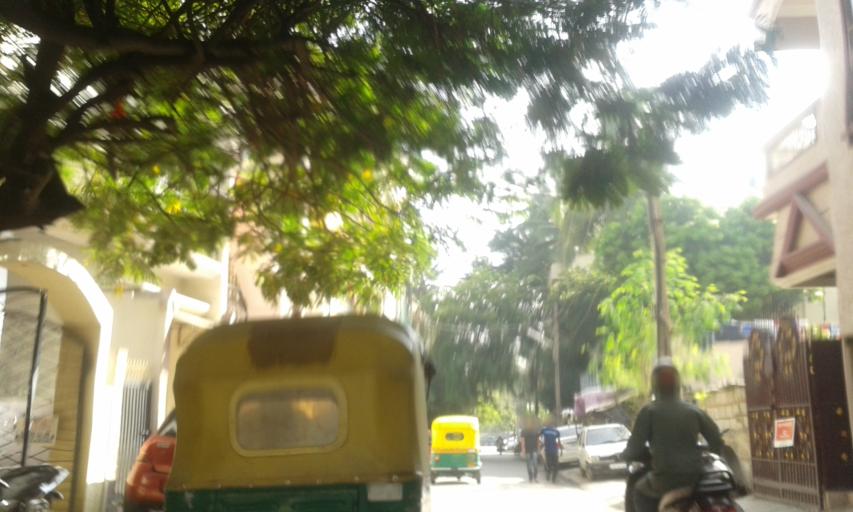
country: IN
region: Karnataka
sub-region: Bangalore Urban
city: Bangalore
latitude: 12.9288
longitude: 77.5992
